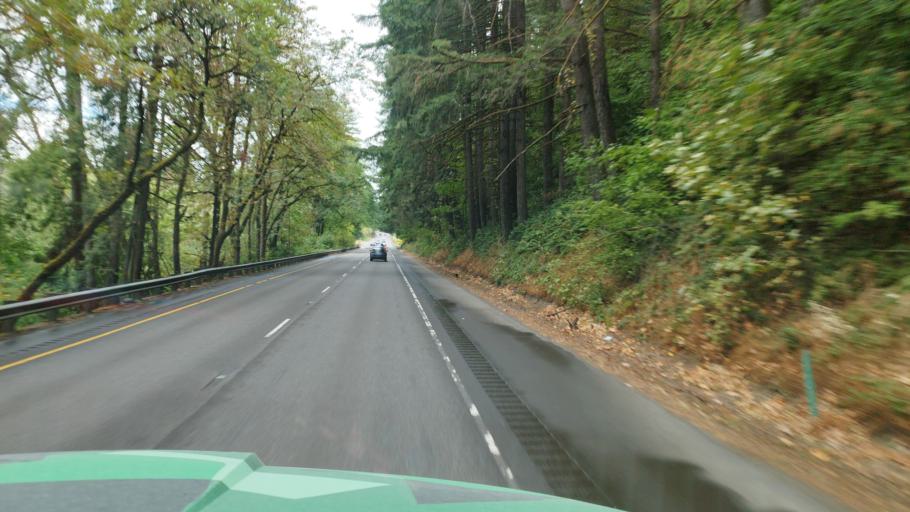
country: US
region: Oregon
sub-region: Washington County
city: Sherwood
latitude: 45.3307
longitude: -122.8837
